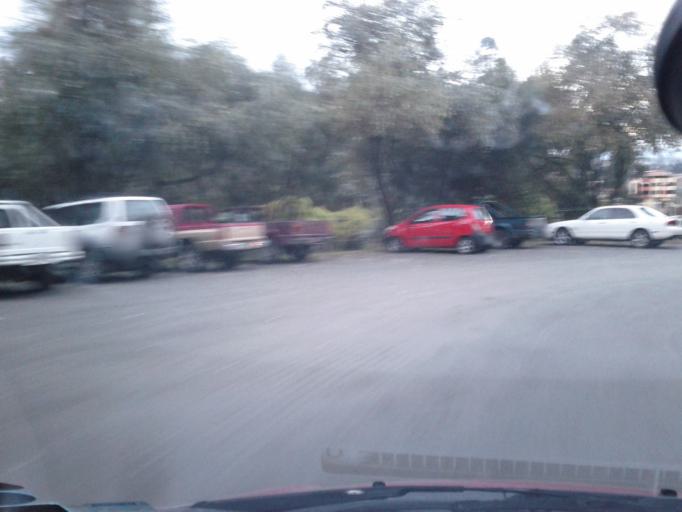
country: EC
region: Azuay
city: Cuenca
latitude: -2.9198
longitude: -79.0249
